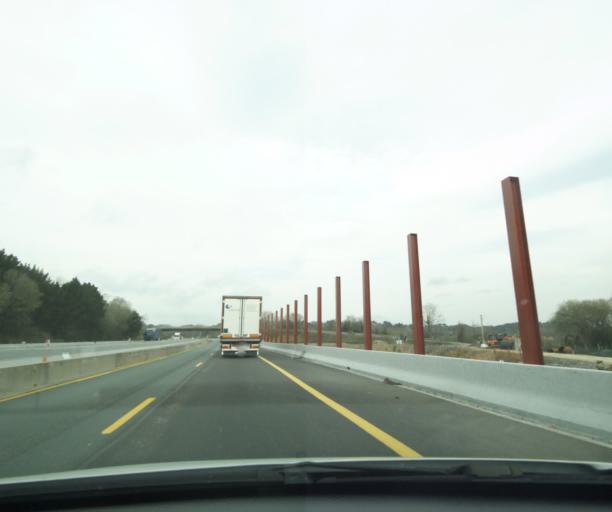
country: FR
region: Aquitaine
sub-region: Departement des Pyrenees-Atlantiques
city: Saint-Jean-de-Luz
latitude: 43.3758
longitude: -1.6488
